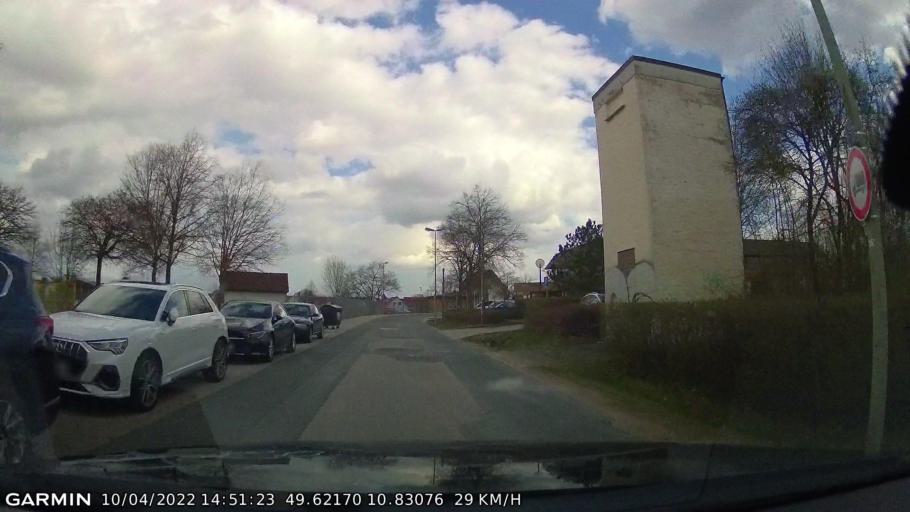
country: DE
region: Bavaria
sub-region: Regierungsbezirk Mittelfranken
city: Weisendorf
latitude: 49.6217
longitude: 10.8309
